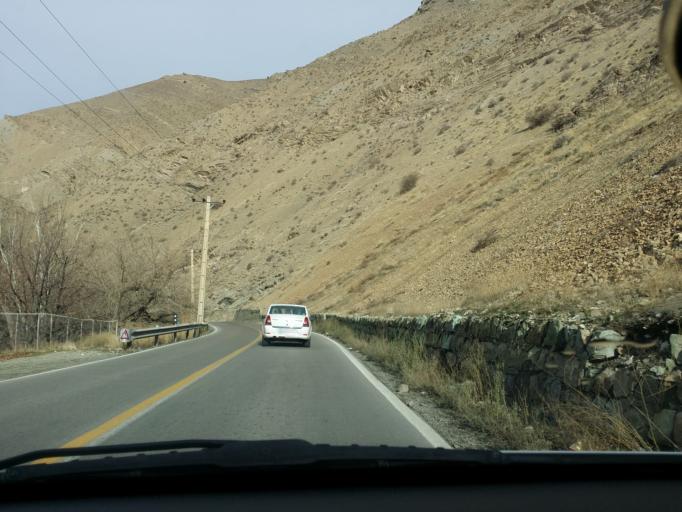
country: IR
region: Tehran
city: Tajrish
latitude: 36.0297
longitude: 51.2357
